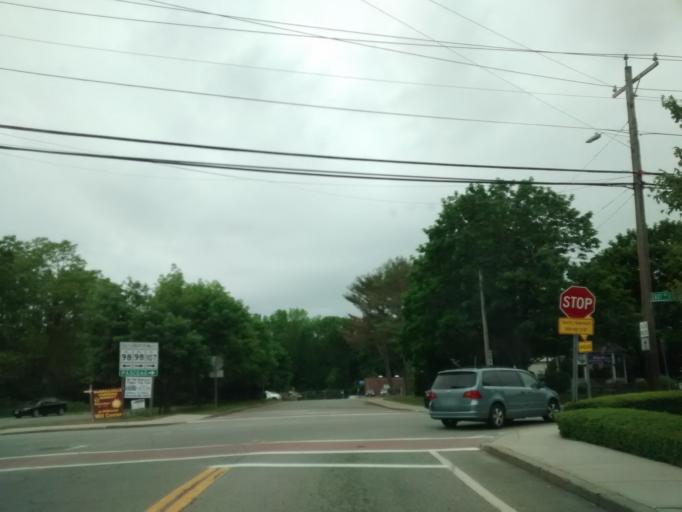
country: US
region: Rhode Island
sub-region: Providence County
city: Harrisville
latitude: 41.9652
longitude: -71.6764
